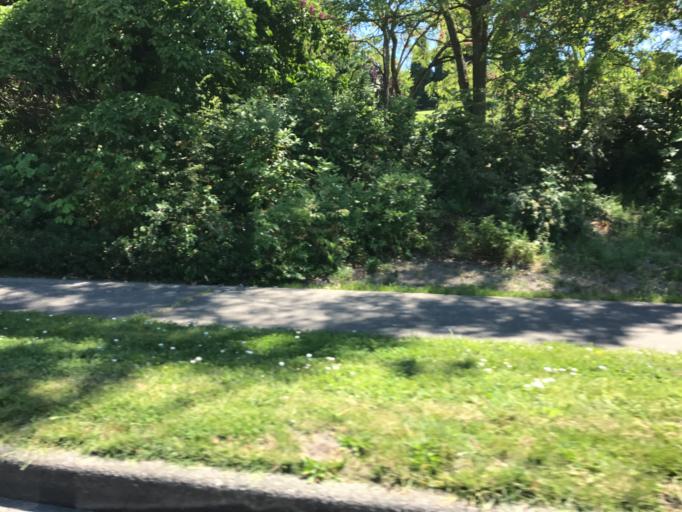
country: US
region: Washington
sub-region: King County
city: Seattle
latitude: 47.5833
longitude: -122.2981
